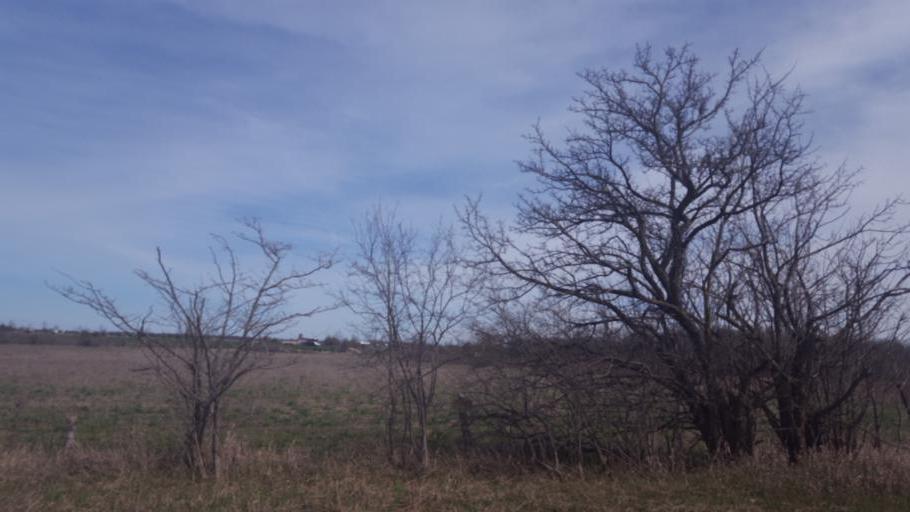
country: US
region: Michigan
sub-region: Gladwin County
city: Gladwin
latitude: 44.0530
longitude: -84.4676
